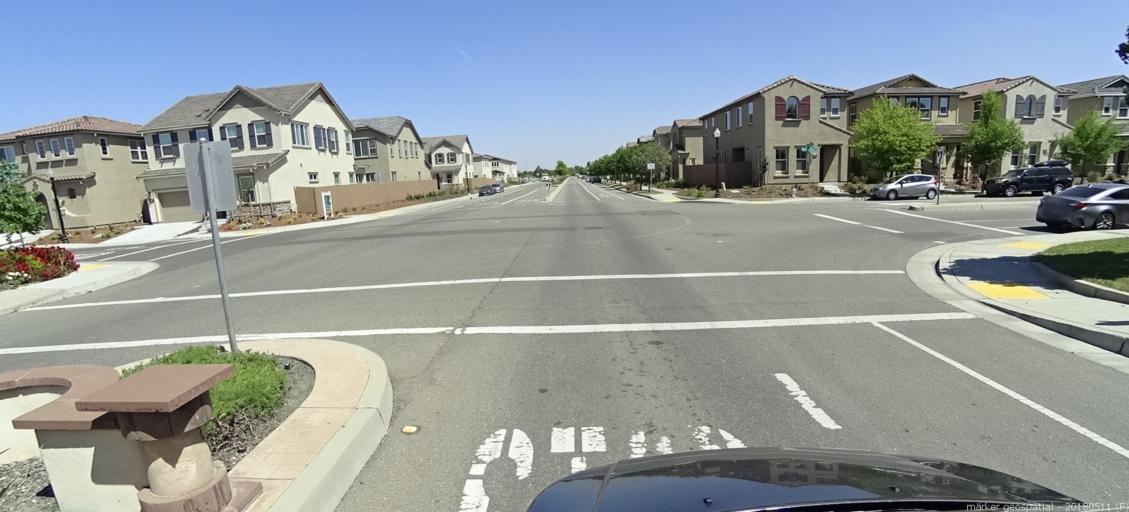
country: US
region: California
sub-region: Yolo County
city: West Sacramento
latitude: 38.6489
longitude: -121.5441
